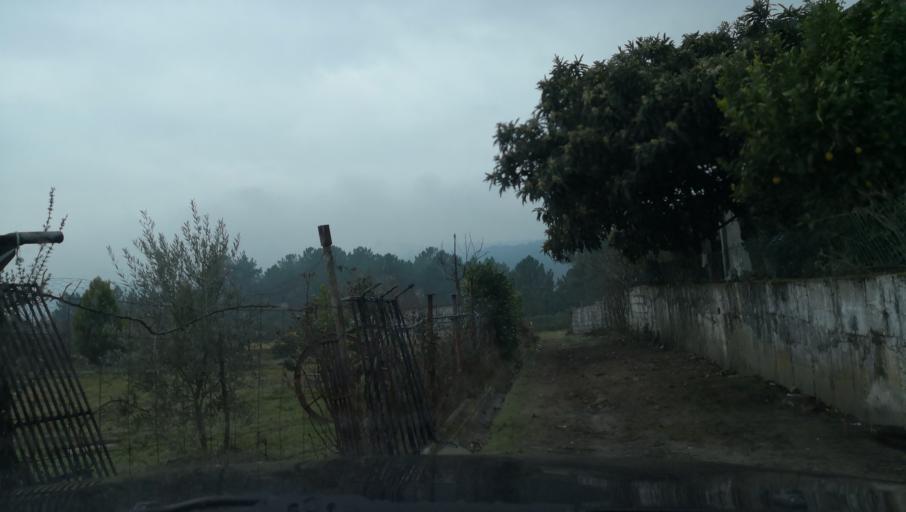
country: PT
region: Vila Real
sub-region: Vila Real
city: Vila Real
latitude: 41.3031
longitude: -7.7844
